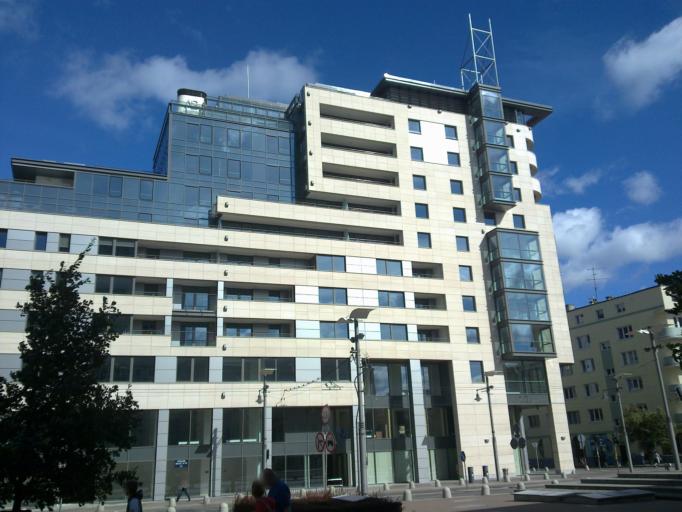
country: PL
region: Pomeranian Voivodeship
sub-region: Gdynia
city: Gdynia
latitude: 54.5221
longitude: 18.5434
